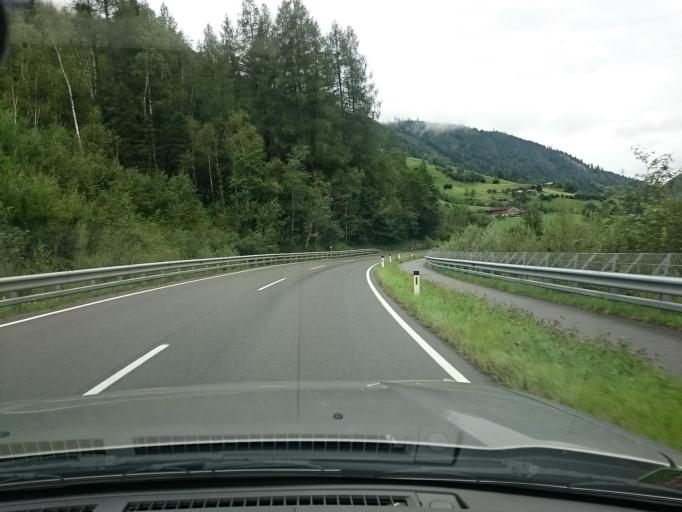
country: AT
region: Salzburg
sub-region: Politischer Bezirk Zell am See
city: Bruck an der Grossglocknerstrasse
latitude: 47.2513
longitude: 12.8251
